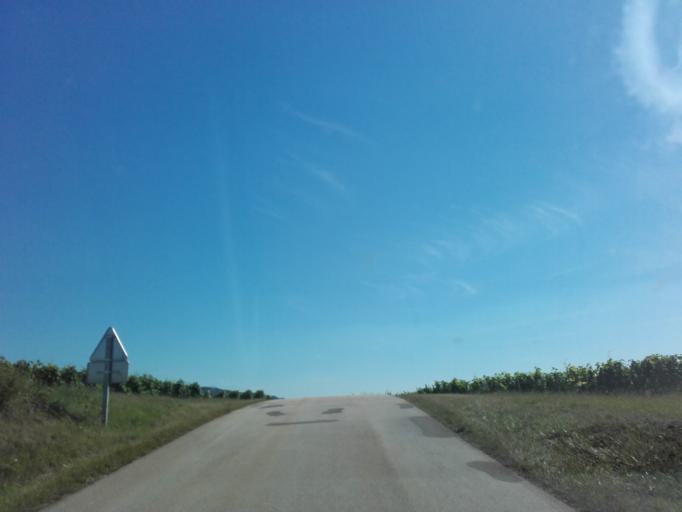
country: FR
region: Bourgogne
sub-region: Departement de Saone-et-Loire
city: Saint-Leger-sur-Dheune
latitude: 46.8982
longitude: 4.6766
